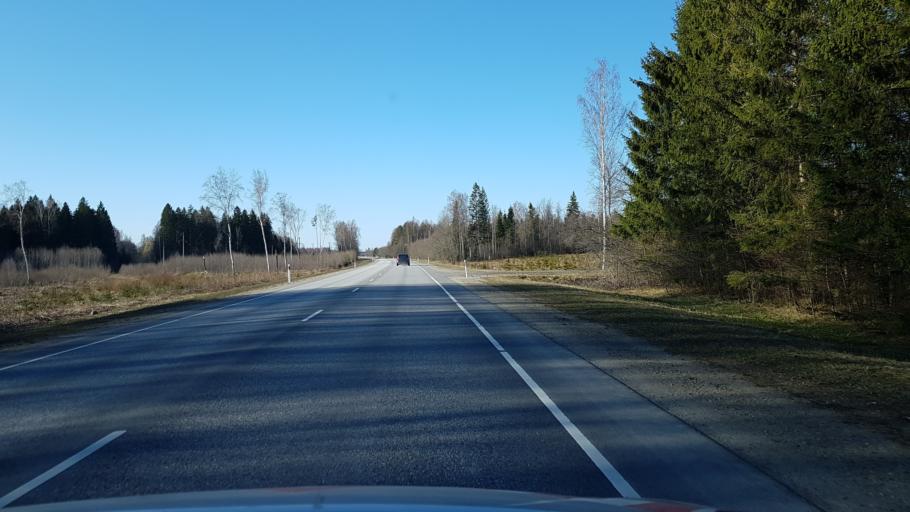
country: EE
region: Ida-Virumaa
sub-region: Johvi vald
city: Johvi
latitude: 59.2019
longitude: 27.3455
